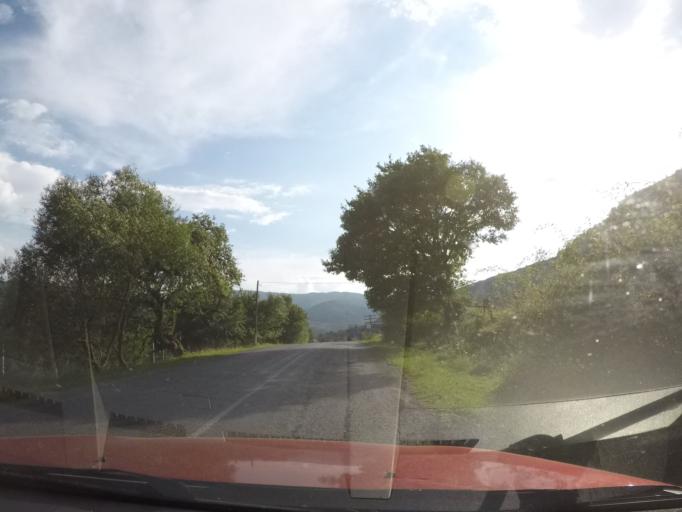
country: UA
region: Zakarpattia
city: Velykyi Bereznyi
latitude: 48.9521
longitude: 22.6095
